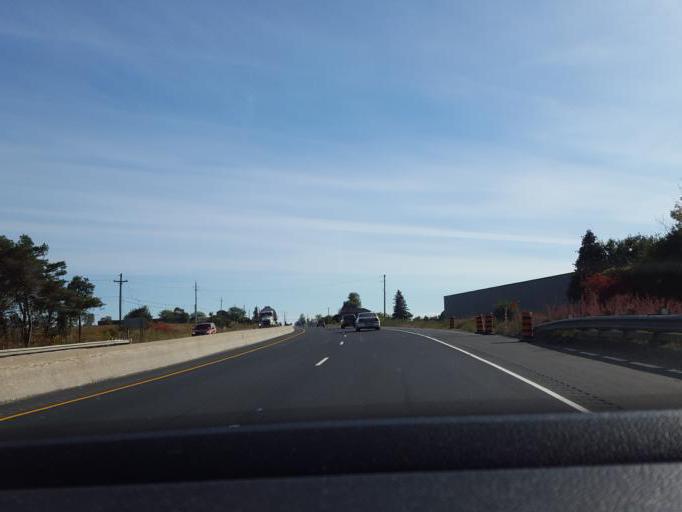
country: CA
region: Ontario
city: Oshawa
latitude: 43.9490
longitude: -78.6059
